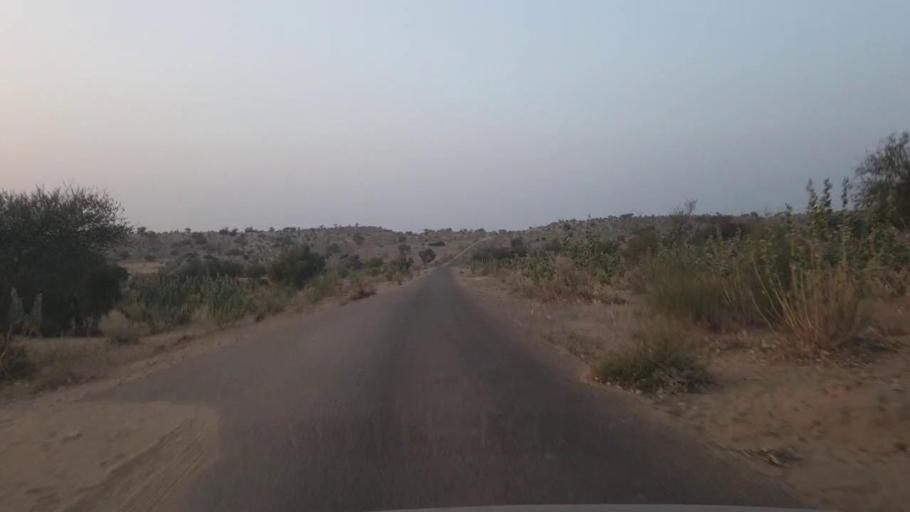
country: PK
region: Sindh
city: Umarkot
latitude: 25.3144
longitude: 70.0596
